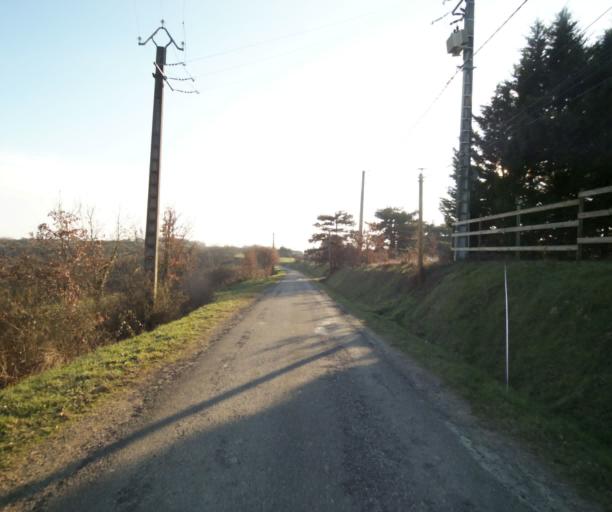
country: FR
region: Midi-Pyrenees
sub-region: Departement du Tarn-et-Garonne
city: Moissac
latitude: 44.1370
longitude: 1.1373
